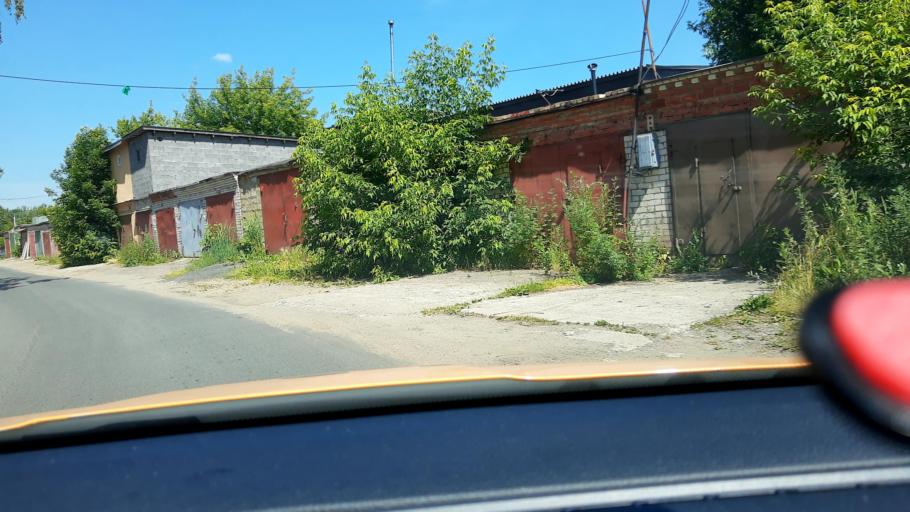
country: RU
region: Moscow
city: Severnyy
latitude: 55.9488
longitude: 37.5303
